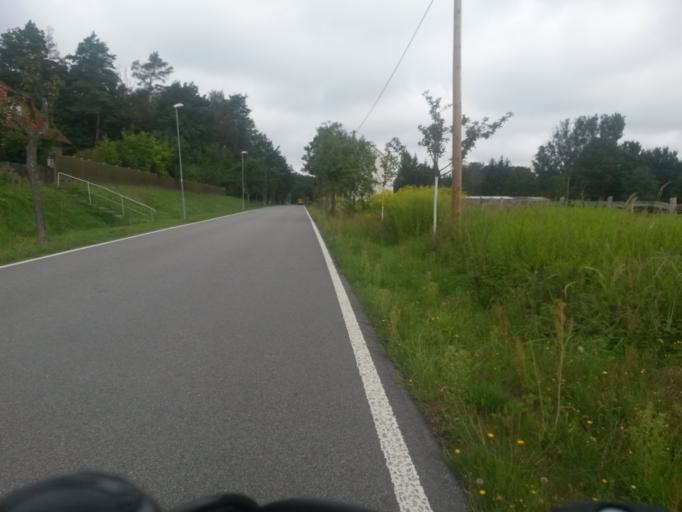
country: DE
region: Brandenburg
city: Angermunde
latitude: 53.0510
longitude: 13.9461
